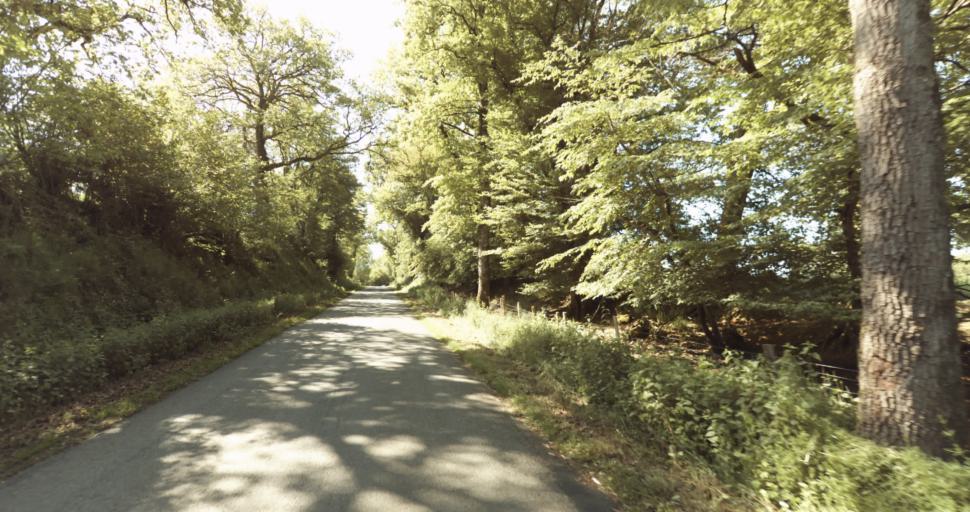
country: FR
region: Limousin
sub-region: Departement de la Haute-Vienne
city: Le Vigen
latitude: 45.7254
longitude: 1.2868
